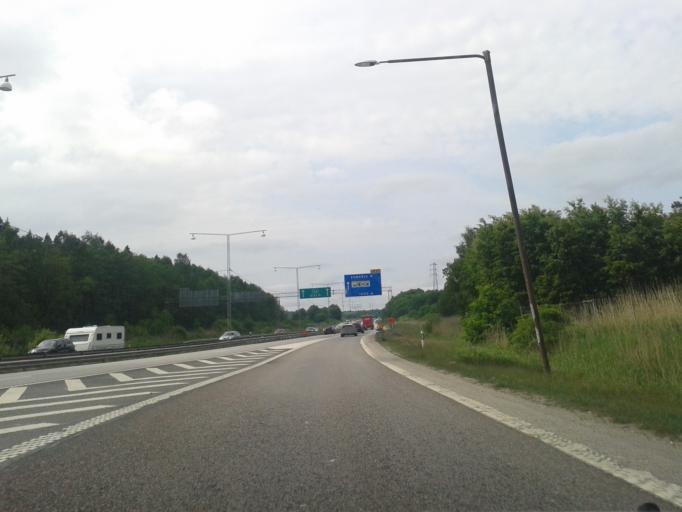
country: SE
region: Vaestra Goetaland
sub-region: Kungalvs Kommun
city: Kungalv
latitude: 57.8775
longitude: 11.9602
